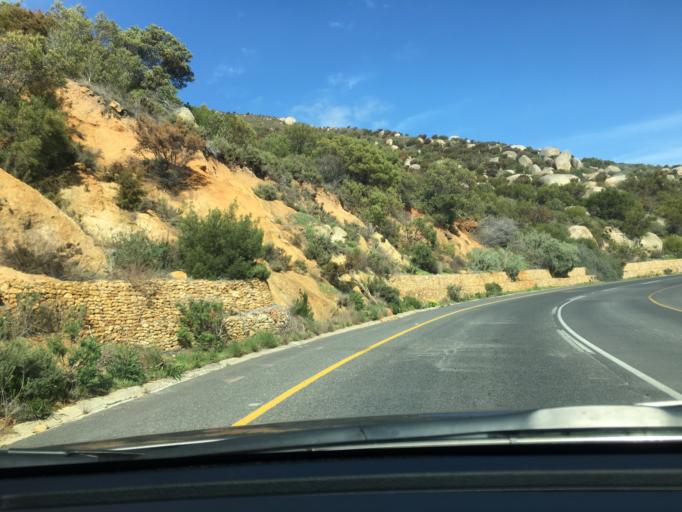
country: ZA
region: Western Cape
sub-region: City of Cape Town
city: Constantia
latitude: -33.9871
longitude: 18.3543
